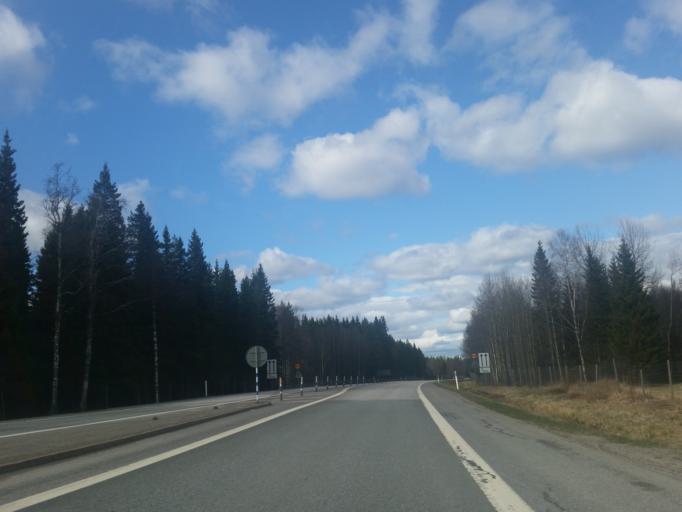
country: SE
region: Vaesterbotten
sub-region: Robertsfors Kommun
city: Robertsfors
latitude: 64.0620
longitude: 20.8480
